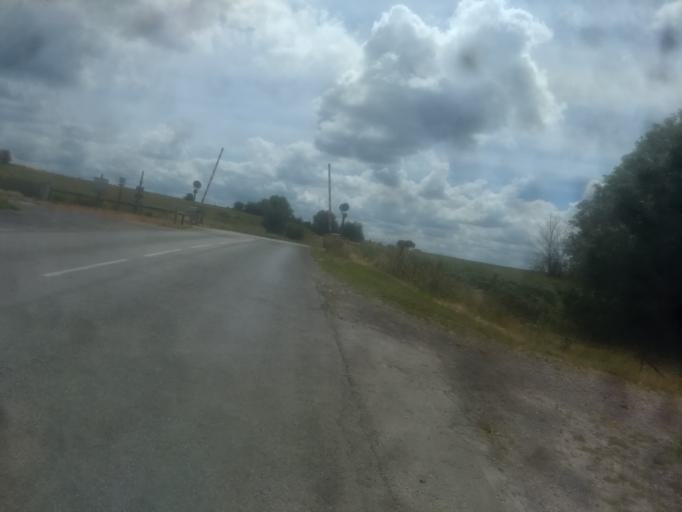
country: FR
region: Nord-Pas-de-Calais
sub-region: Departement du Pas-de-Calais
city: Mont-Saint-Eloi
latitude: 50.3442
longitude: 2.6505
